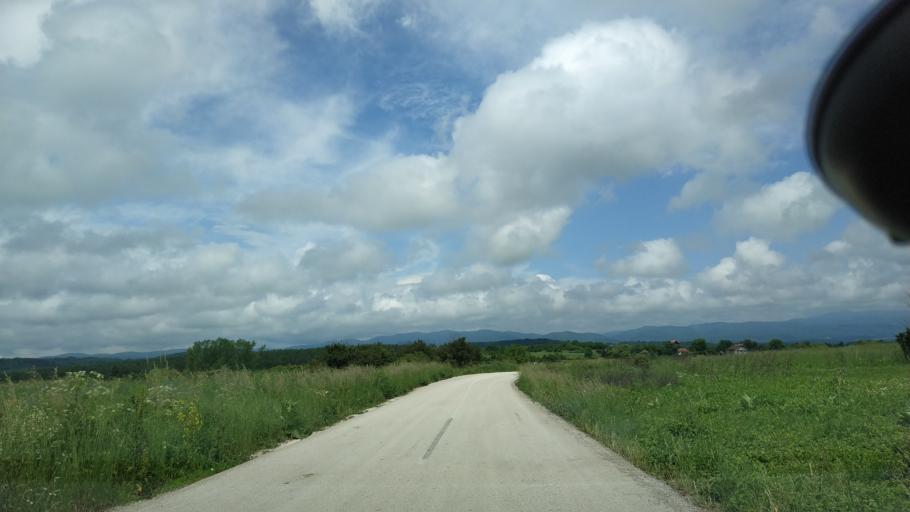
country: RS
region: Central Serbia
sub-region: Zajecarski Okrug
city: Boljevac
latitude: 43.8141
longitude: 21.9527
